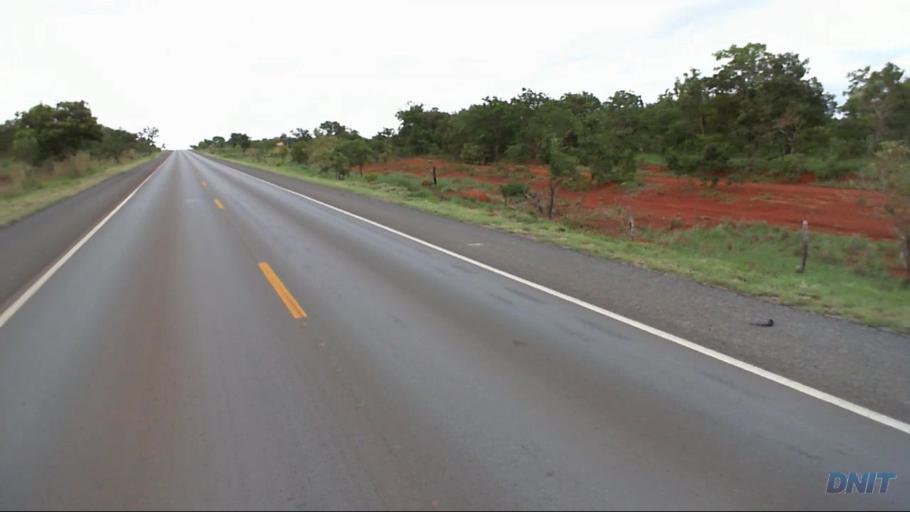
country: BR
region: Goias
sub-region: Barro Alto
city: Barro Alto
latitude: -15.2092
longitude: -48.6807
